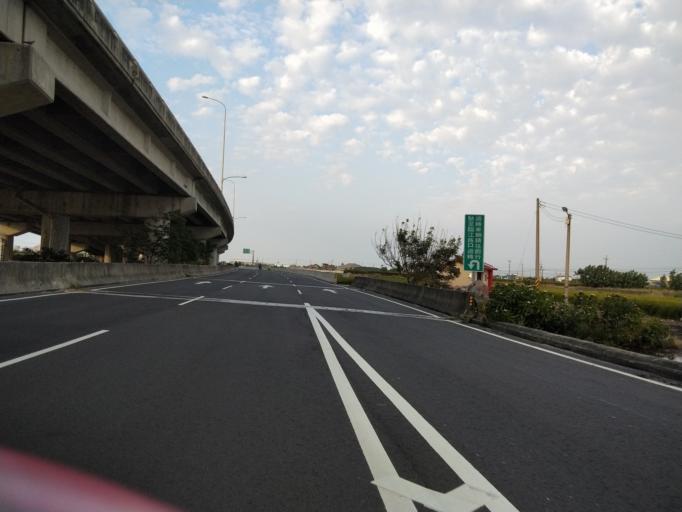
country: TW
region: Taiwan
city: Fengyuan
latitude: 24.4054
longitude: 120.6138
